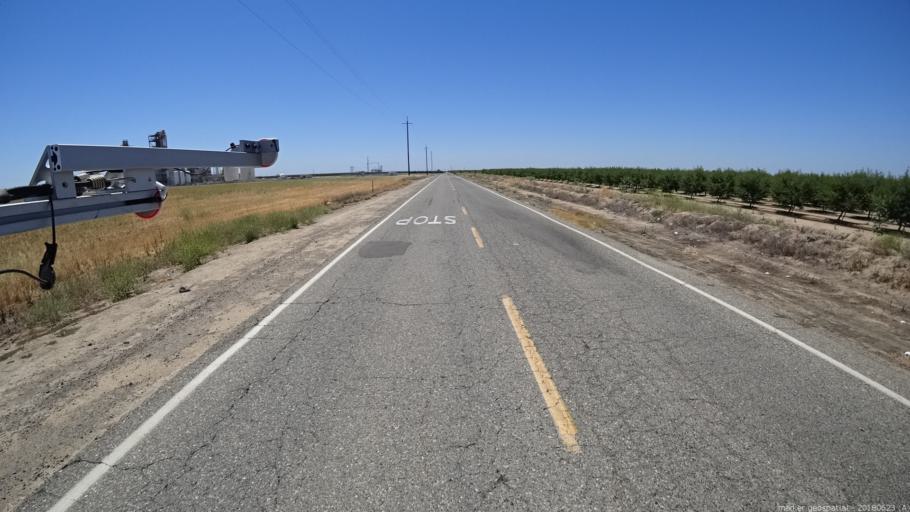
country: US
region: California
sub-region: Madera County
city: Chowchilla
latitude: 37.0961
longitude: -120.2294
